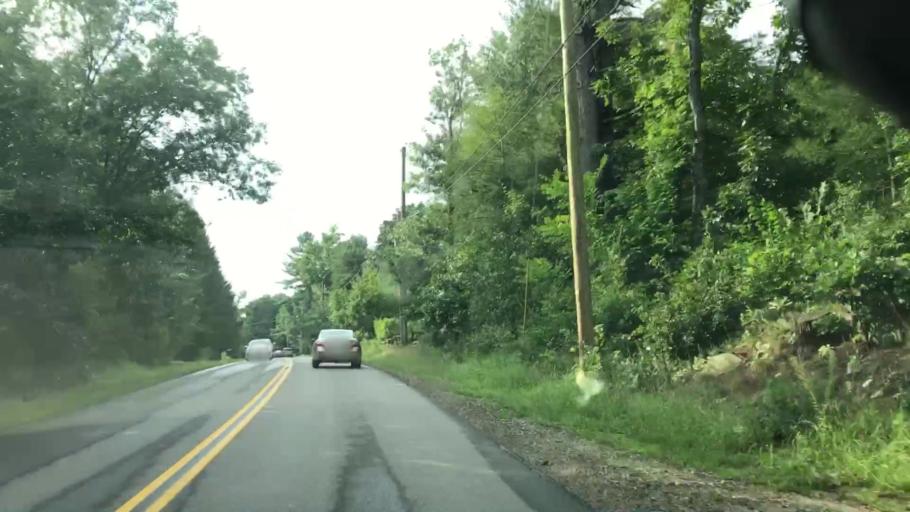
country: US
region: New Hampshire
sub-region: Hillsborough County
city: Milford
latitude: 42.8282
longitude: -71.5864
